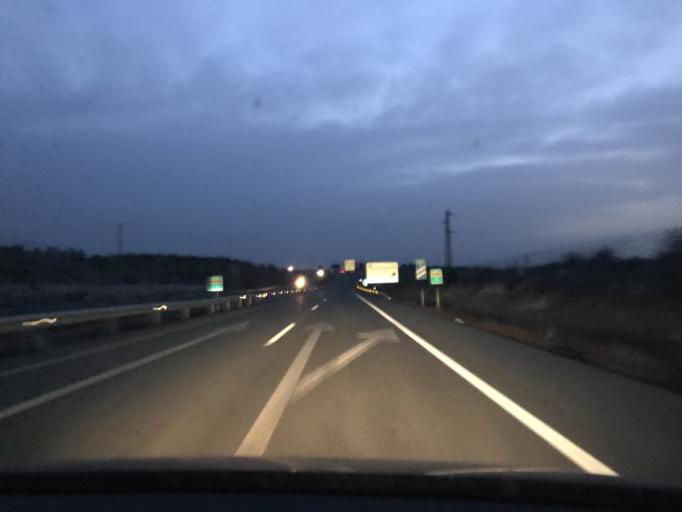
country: ES
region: Andalusia
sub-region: Provincia de Granada
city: Gor
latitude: 37.3973
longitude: -2.9817
